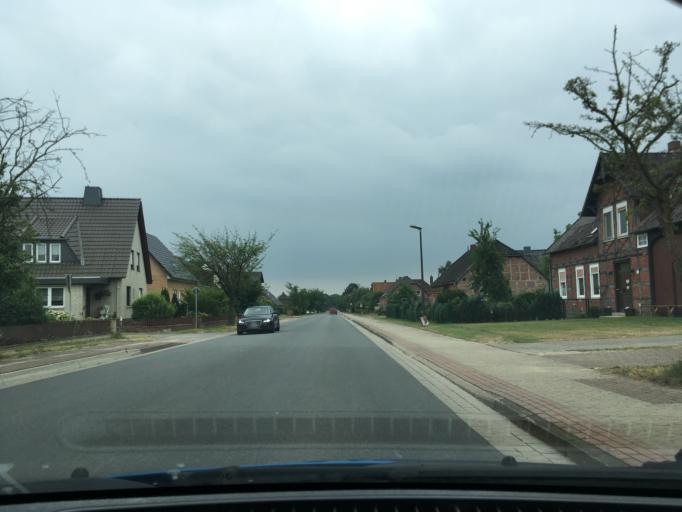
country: DE
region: Lower Saxony
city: Lubbow
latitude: 52.9146
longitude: 11.1803
